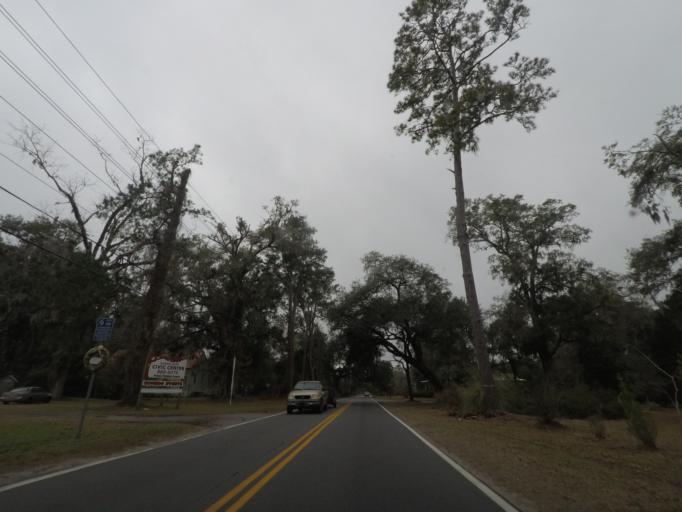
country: US
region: South Carolina
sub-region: Charleston County
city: Hollywood
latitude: 32.7190
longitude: -80.3487
